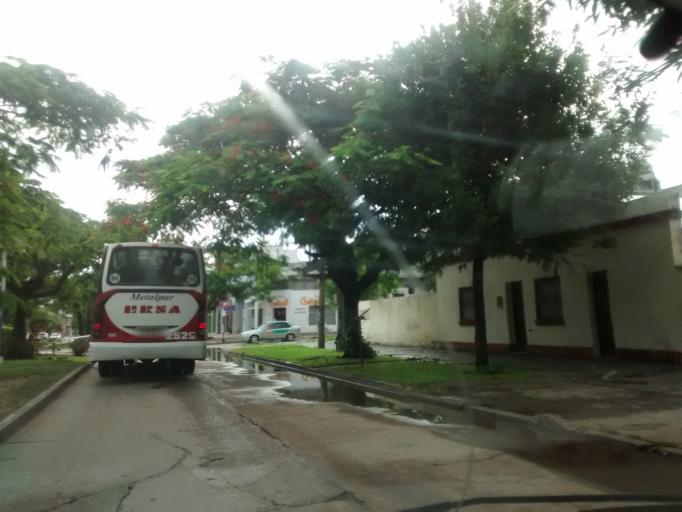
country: AR
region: Chaco
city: Resistencia
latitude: -27.4524
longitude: -58.9967
